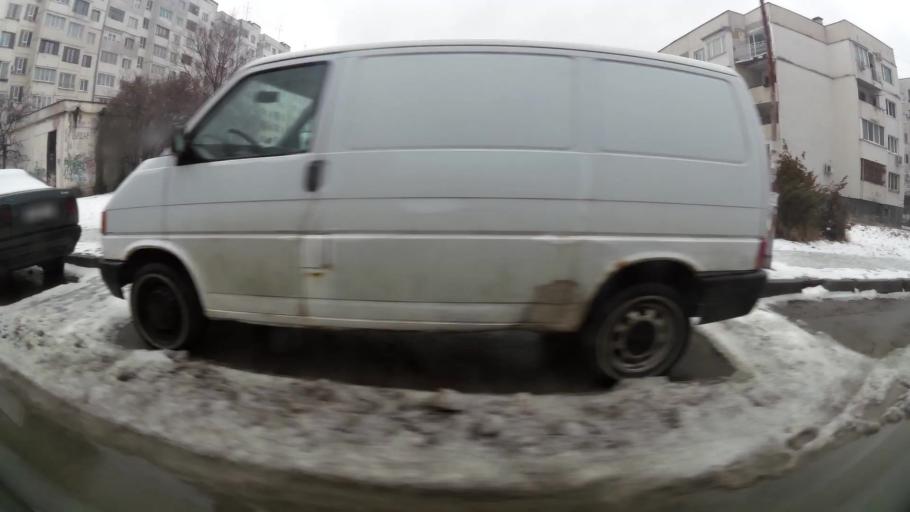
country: BG
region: Sofia-Capital
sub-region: Stolichna Obshtina
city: Sofia
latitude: 42.6870
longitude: 23.2605
